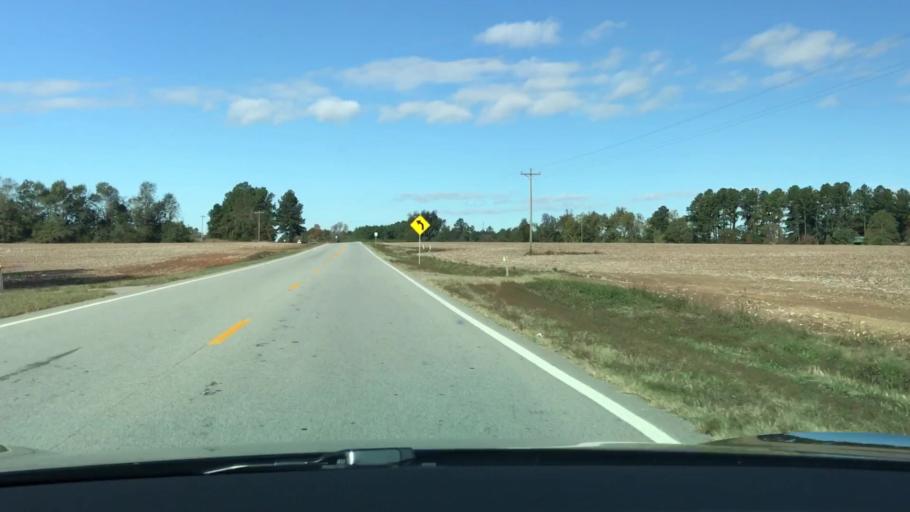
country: US
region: Georgia
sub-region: Jefferson County
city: Wrens
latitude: 33.2569
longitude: -82.4701
